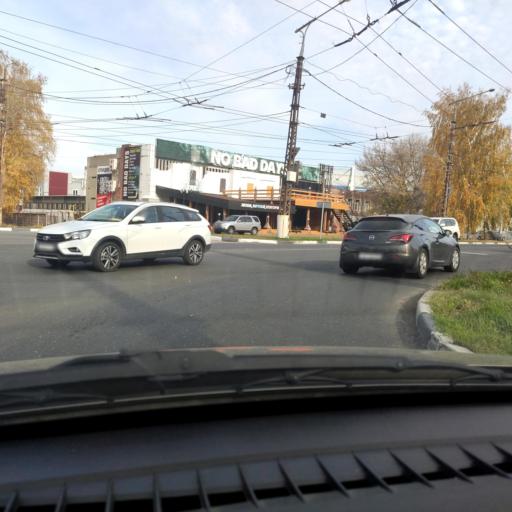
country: RU
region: Samara
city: Tol'yatti
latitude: 53.4988
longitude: 49.3888
